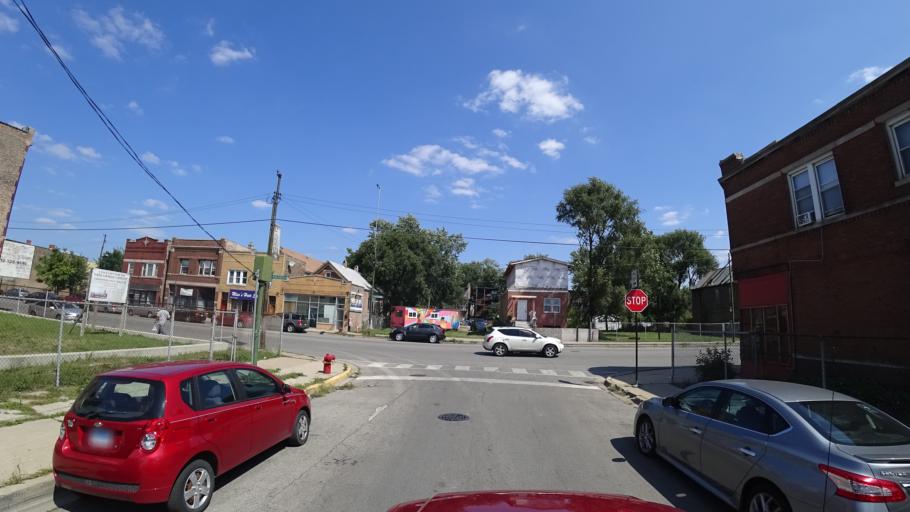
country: US
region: Illinois
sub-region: Cook County
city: Cicero
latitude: 41.8526
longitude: -87.7251
